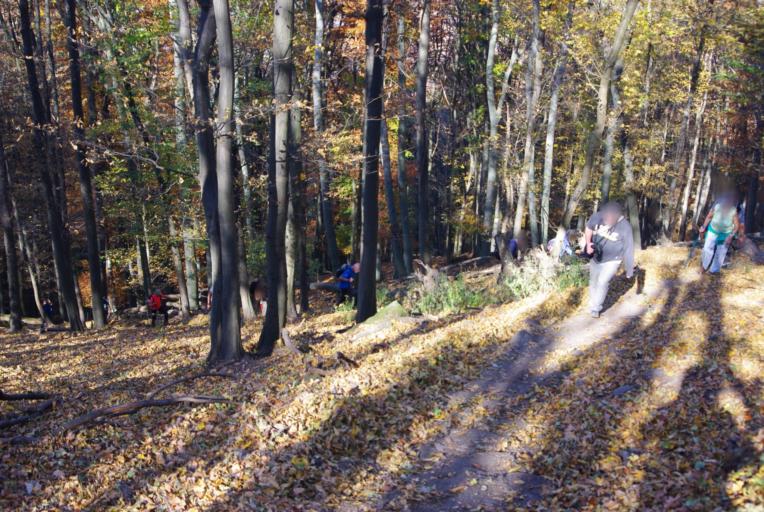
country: HU
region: Pest
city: Pilisszentkereszt
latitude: 47.7381
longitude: 18.9158
